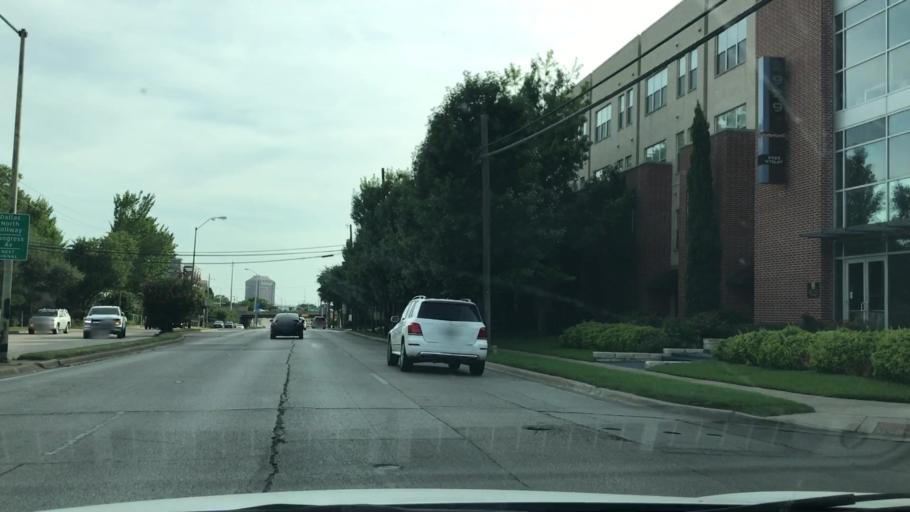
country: US
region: Texas
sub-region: Dallas County
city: Highland Park
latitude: 32.8132
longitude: -96.8157
